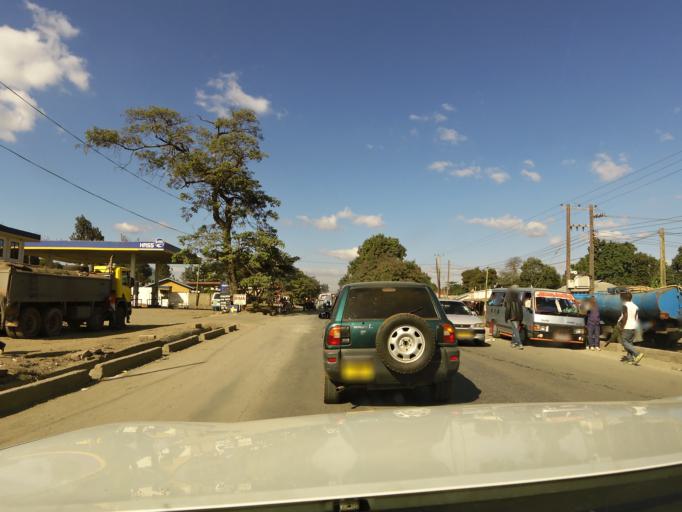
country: TZ
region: Arusha
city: Arusha
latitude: -3.3761
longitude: 36.6623
